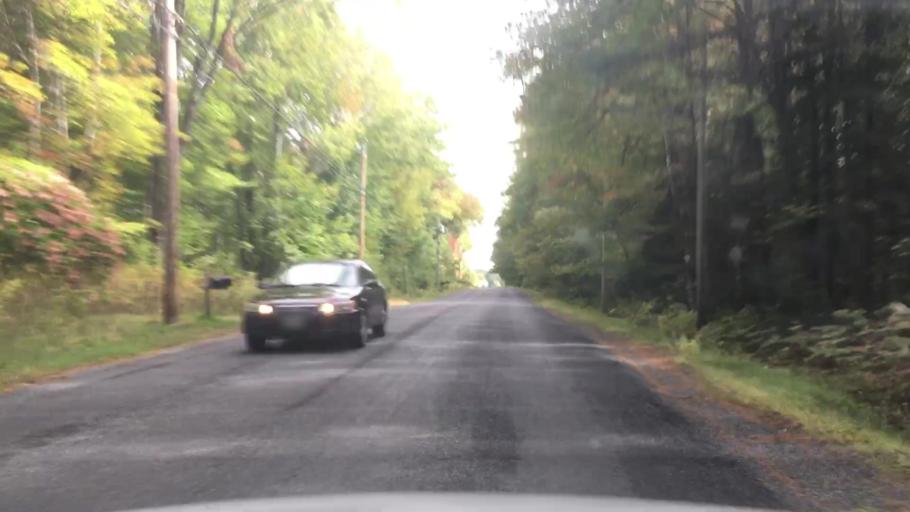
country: US
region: Maine
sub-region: Androscoggin County
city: Lisbon Falls
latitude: 43.9685
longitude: -70.0700
